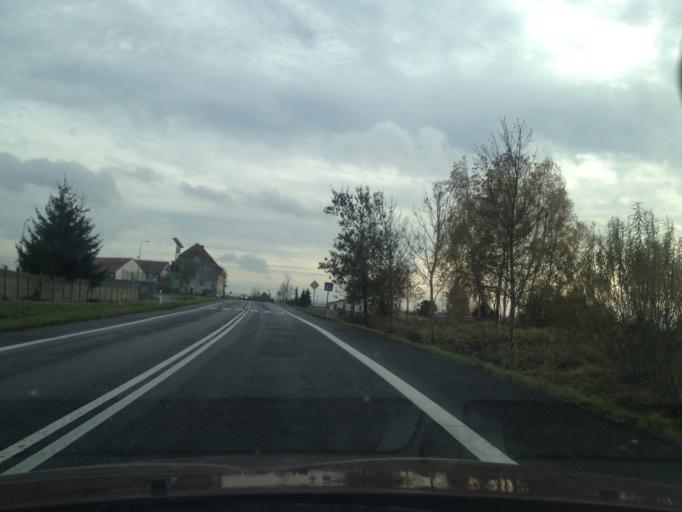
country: PL
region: Lower Silesian Voivodeship
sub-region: Powiat lubanski
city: Pisarzowice
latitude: 51.1383
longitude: 15.2366
